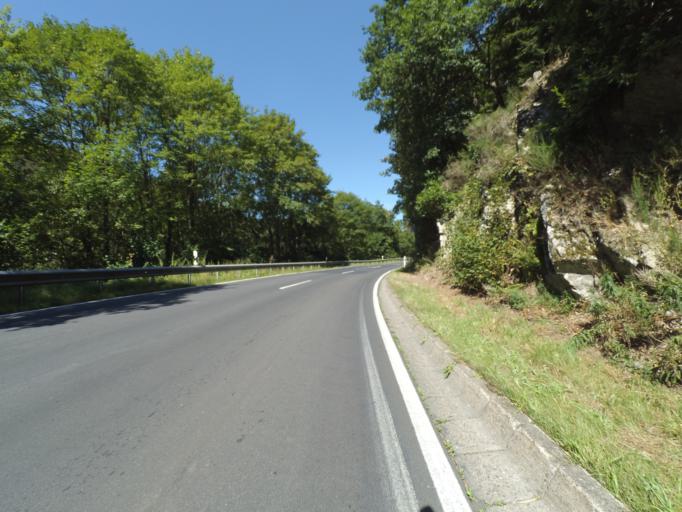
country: DE
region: Rheinland-Pfalz
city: Mullenbach
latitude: 50.2041
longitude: 7.0602
